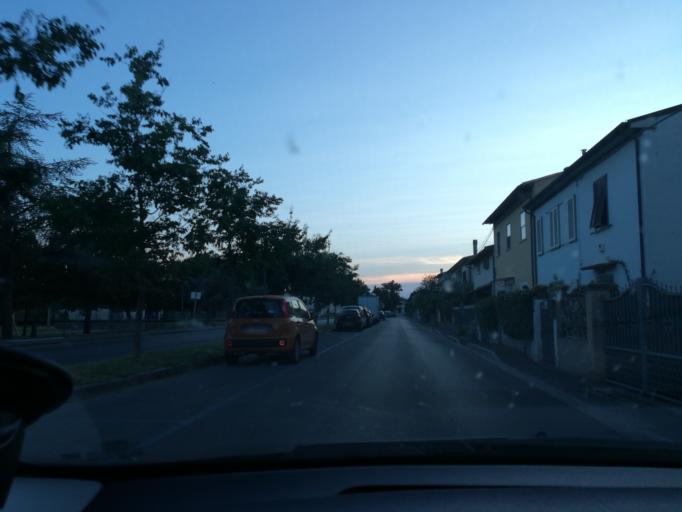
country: IT
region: Tuscany
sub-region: Province of Pisa
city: Pisa
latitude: 43.7276
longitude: 10.3920
